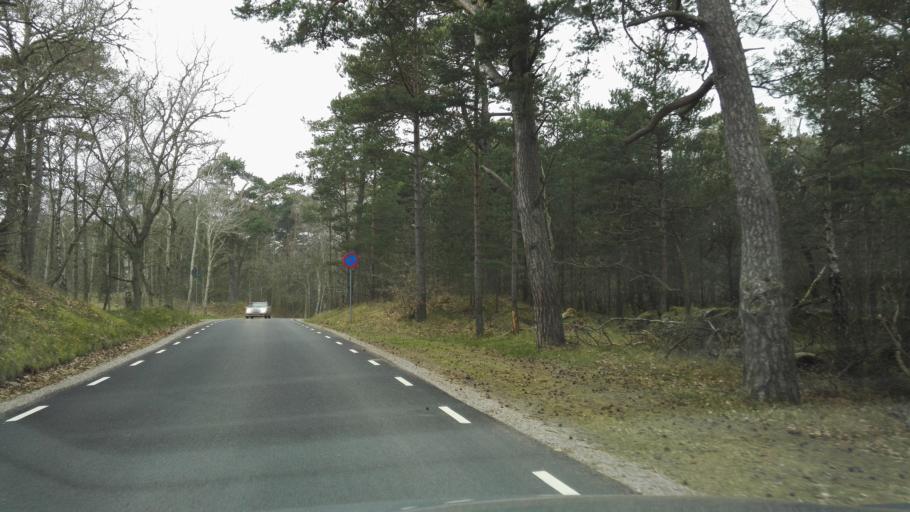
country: SE
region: Skane
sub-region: Simrishamns Kommun
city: Simrishamn
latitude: 55.3882
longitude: 14.1921
